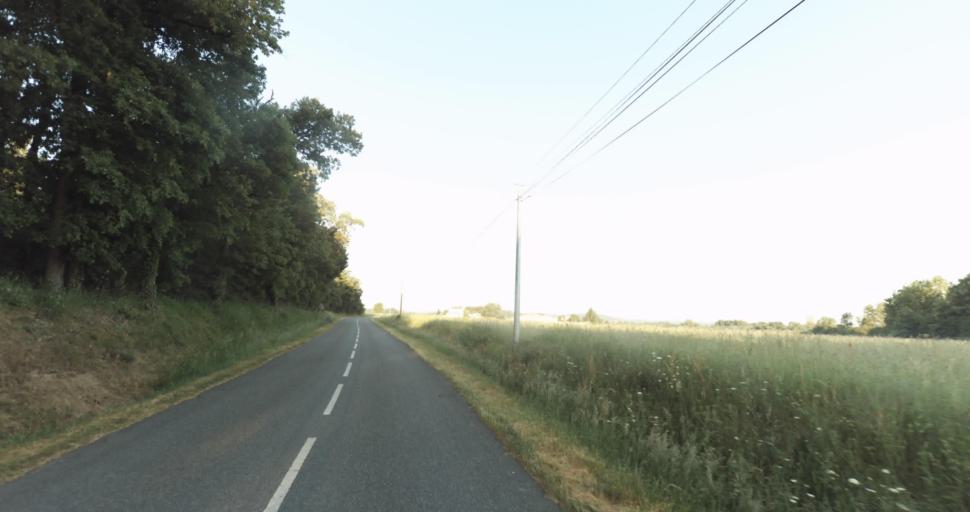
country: FR
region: Midi-Pyrenees
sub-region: Departement de la Haute-Garonne
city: Leguevin
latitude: 43.5811
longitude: 1.2135
